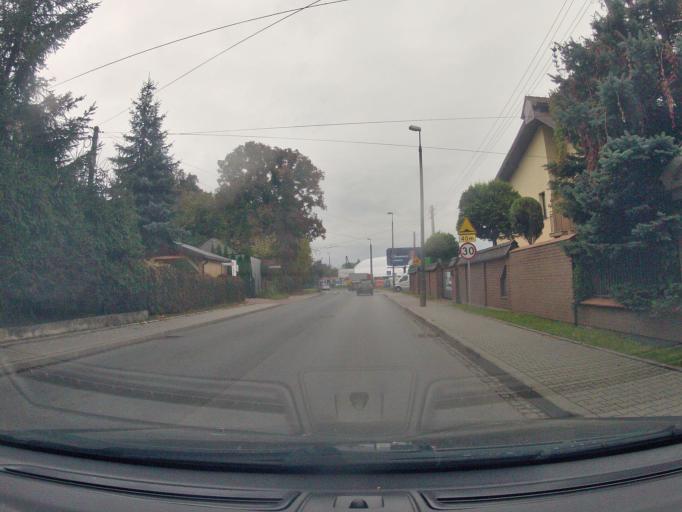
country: PL
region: Lesser Poland Voivodeship
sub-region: Powiat krakowski
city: Rzaska
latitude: 50.0768
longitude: 19.8813
